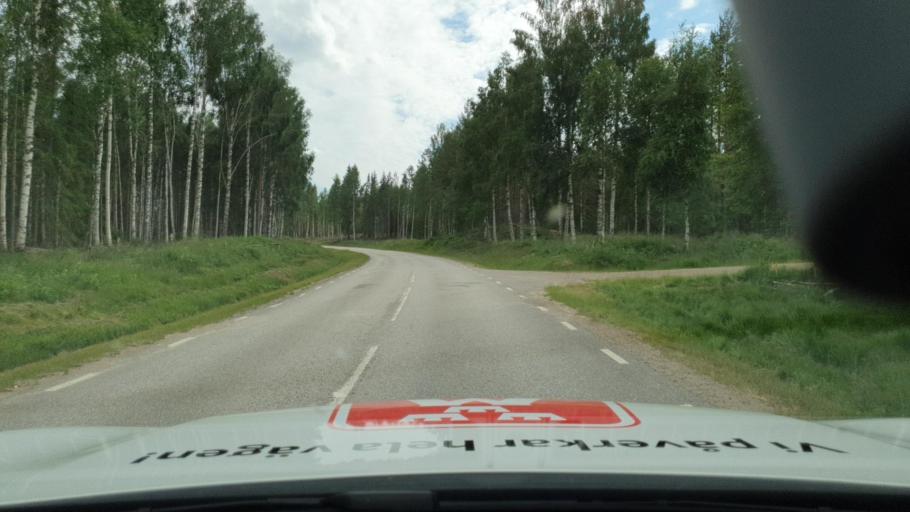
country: NO
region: Hedmark
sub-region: Trysil
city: Innbygda
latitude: 61.0278
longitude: 12.4679
